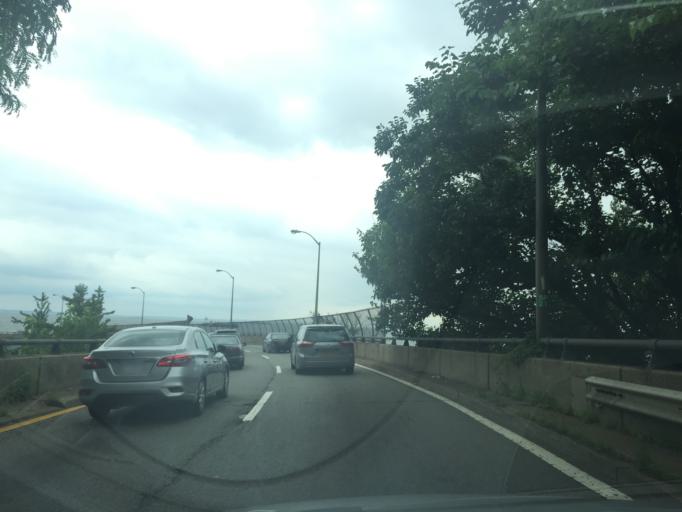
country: US
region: New York
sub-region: Kings County
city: Bensonhurst
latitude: 40.6093
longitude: -74.0342
